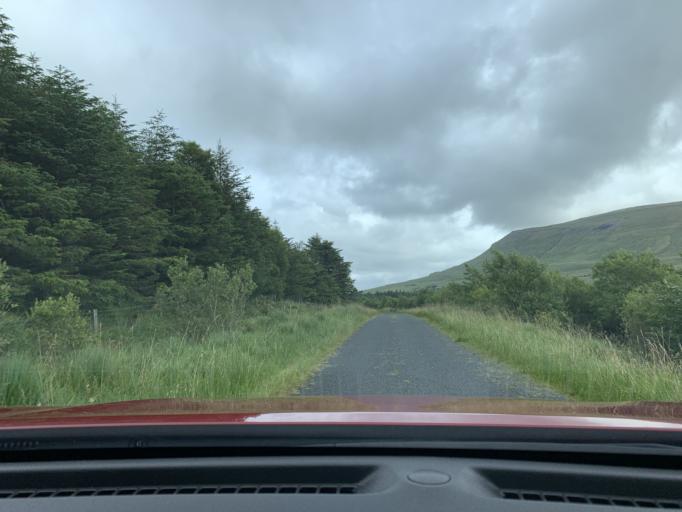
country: IE
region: Connaught
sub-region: Sligo
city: Sligo
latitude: 54.3852
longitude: -8.4084
